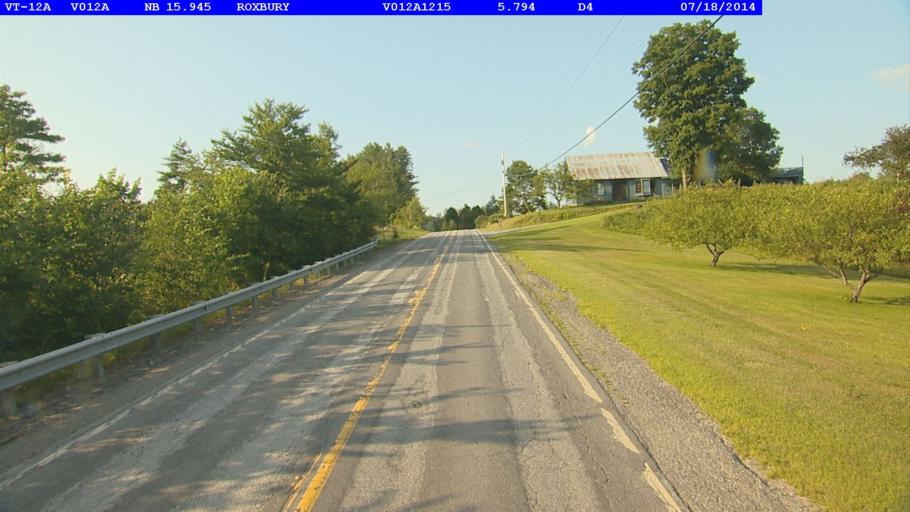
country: US
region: Vermont
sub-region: Washington County
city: Northfield
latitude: 44.1083
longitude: -72.7278
